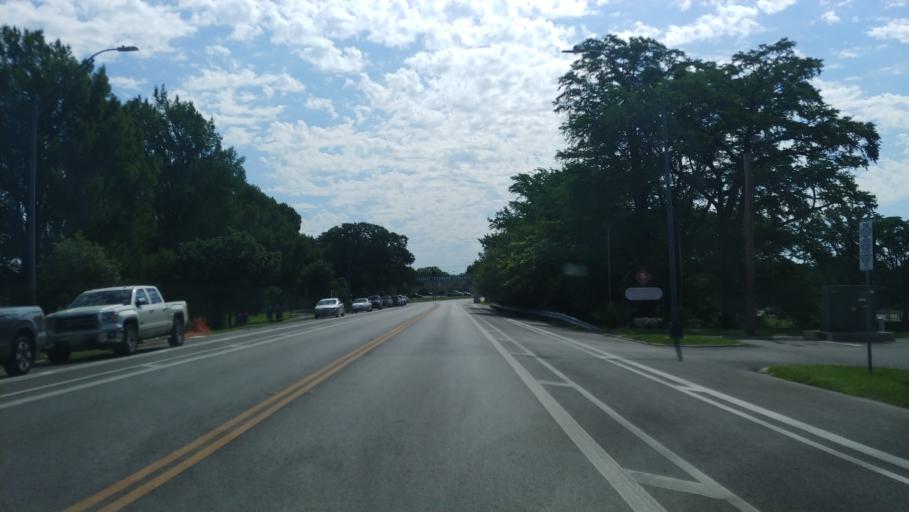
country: US
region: Texas
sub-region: Bexar County
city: Balcones Heights
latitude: 29.4495
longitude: -98.5299
